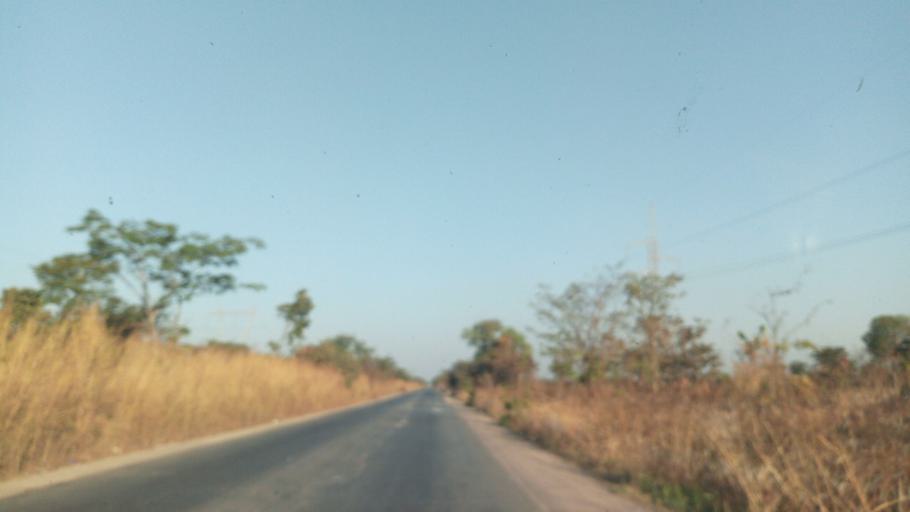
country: CD
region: Katanga
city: Likasi
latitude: -11.1126
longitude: 27.0242
